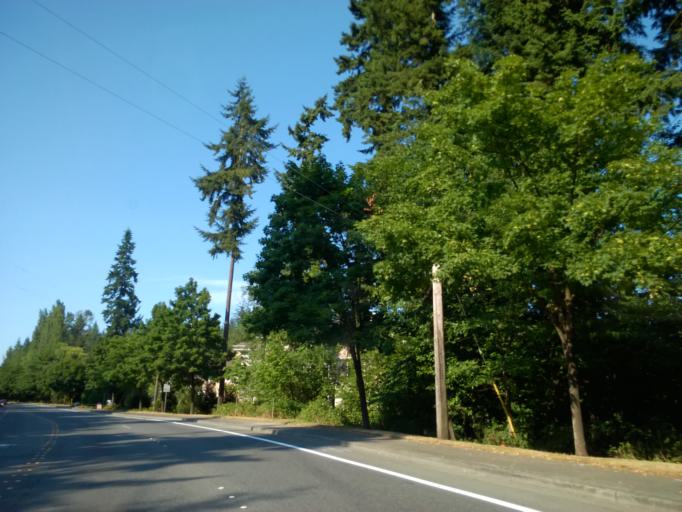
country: US
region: Washington
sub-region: King County
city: Redmond
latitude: 47.6886
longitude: -122.0925
